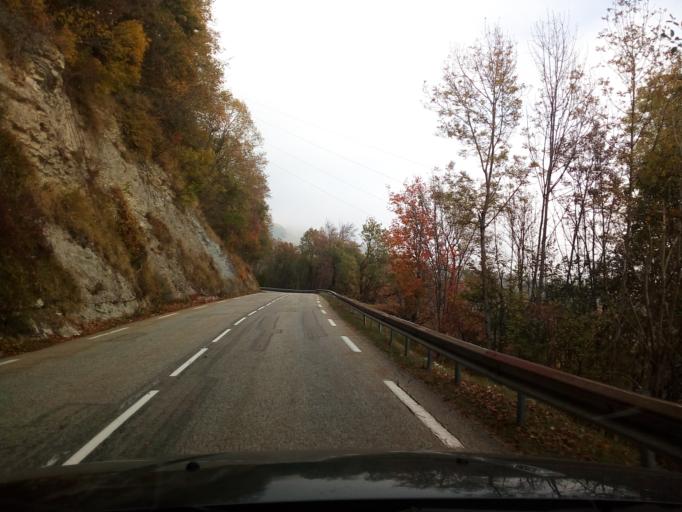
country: FR
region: Rhone-Alpes
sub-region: Departement de l'Isere
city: Bernin
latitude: 45.2871
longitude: 5.8503
